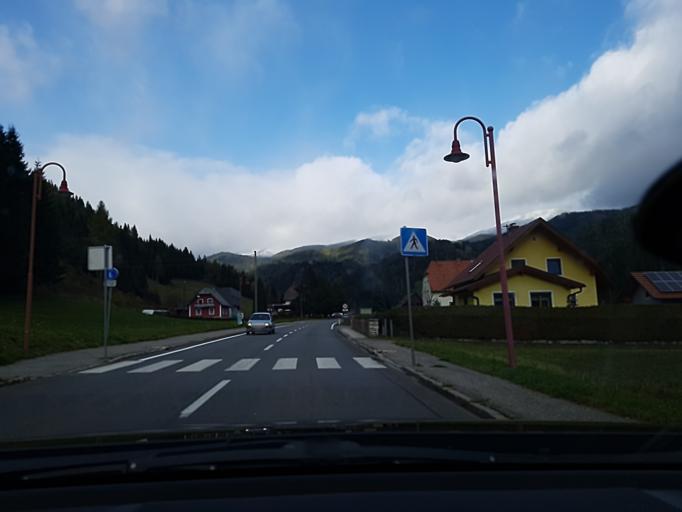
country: AT
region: Styria
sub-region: Politischer Bezirk Murtal
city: Oberzeiring
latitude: 47.2862
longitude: 14.4833
